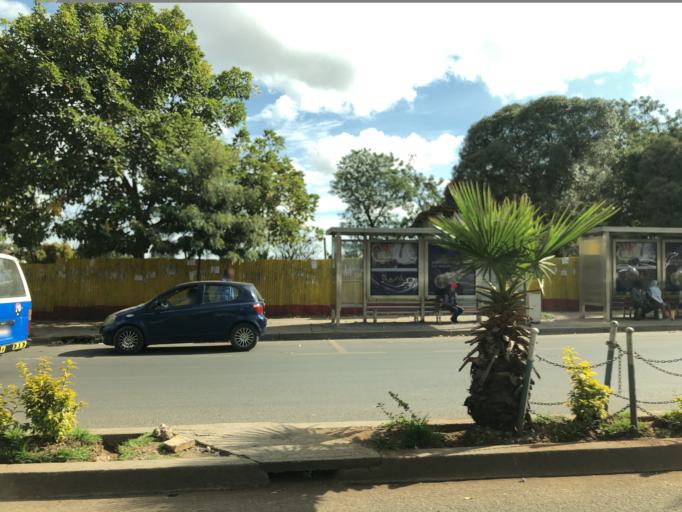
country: ET
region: Adis Abeba
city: Addis Ababa
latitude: 9.0324
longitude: 38.7730
